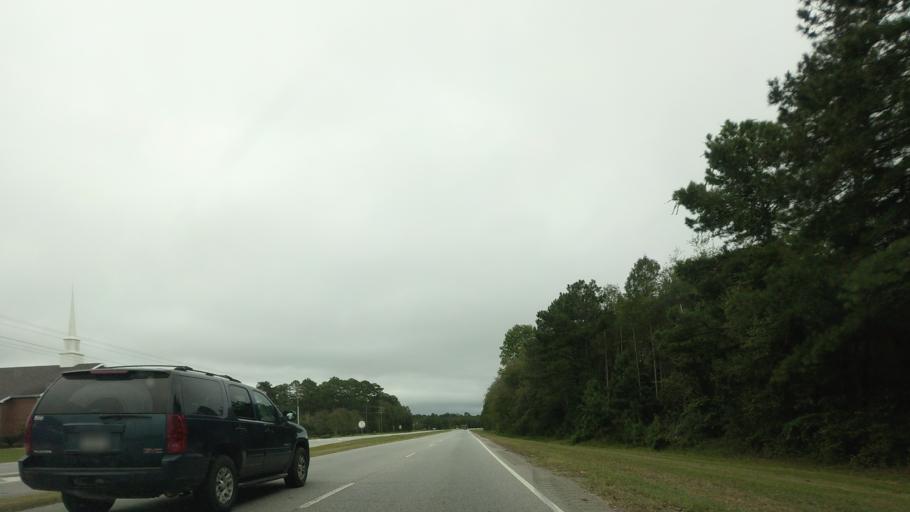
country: US
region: Georgia
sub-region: Lowndes County
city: Valdosta
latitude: 30.8815
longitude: -83.2496
